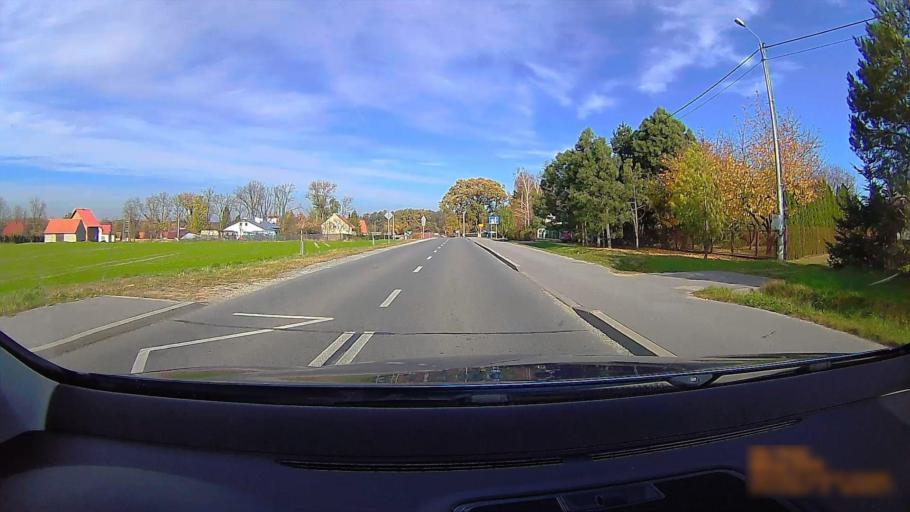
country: PL
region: Greater Poland Voivodeship
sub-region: Powiat ostrzeszowski
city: Doruchow
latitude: 51.3575
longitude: 18.0300
